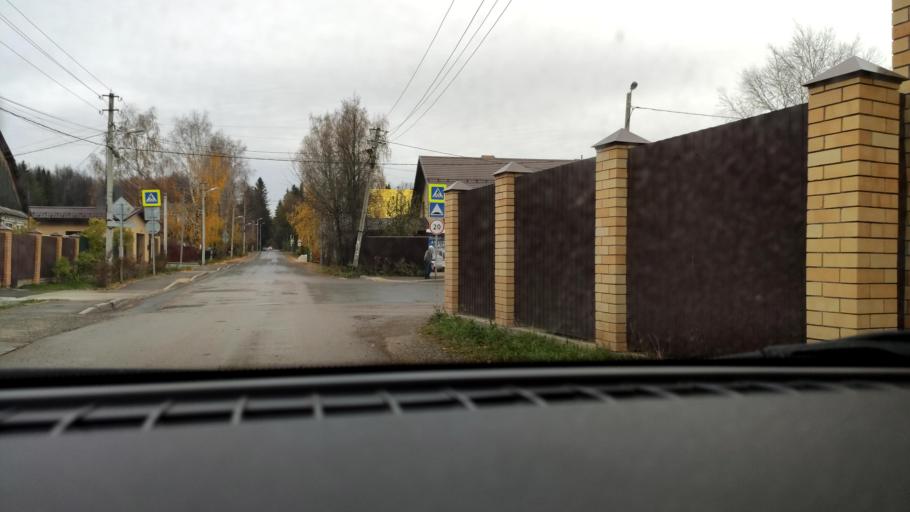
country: RU
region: Perm
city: Froly
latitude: 57.9506
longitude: 56.2995
